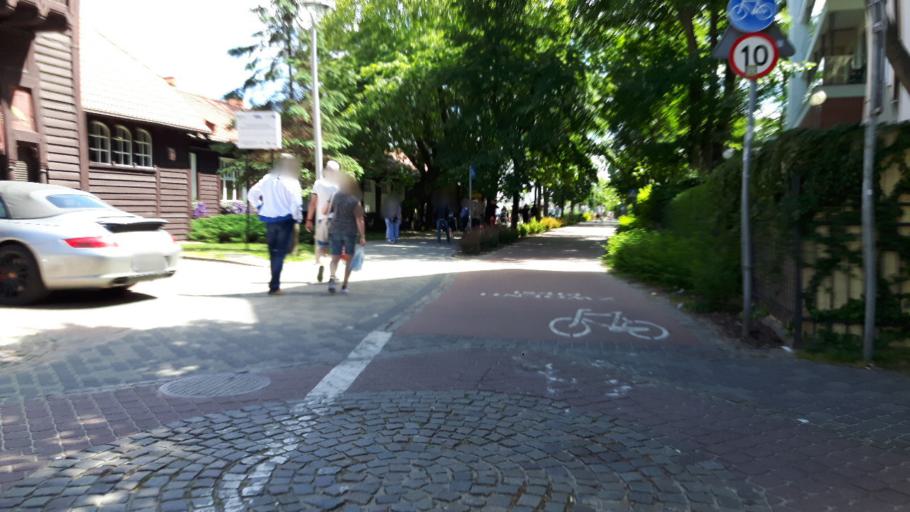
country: PL
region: Pomeranian Voivodeship
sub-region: Sopot
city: Sopot
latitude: 54.4432
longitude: 18.5732
